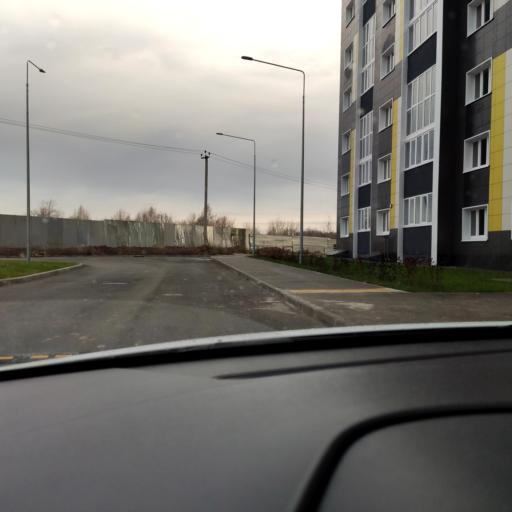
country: RU
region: Tatarstan
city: Osinovo
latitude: 55.8594
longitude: 48.9032
